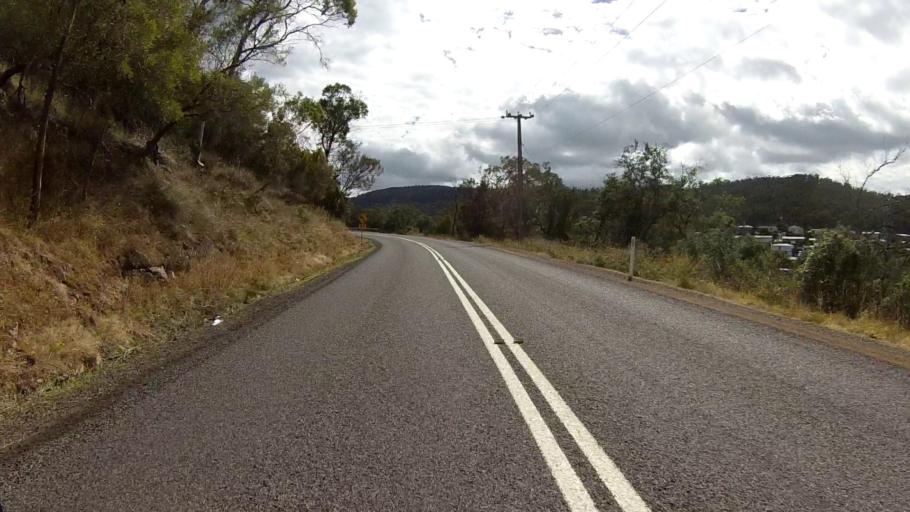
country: AU
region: Tasmania
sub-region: Clarence
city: Lindisfarne
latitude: -42.8075
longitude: 147.3531
